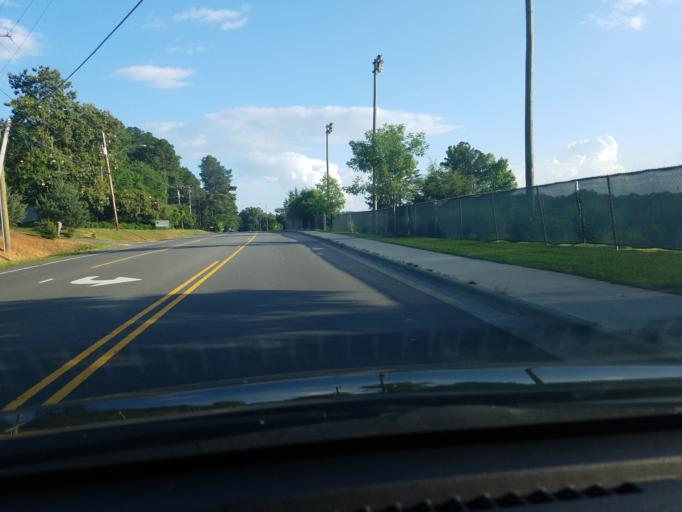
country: US
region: North Carolina
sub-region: Durham County
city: Durham
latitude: 35.9254
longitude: -78.9609
